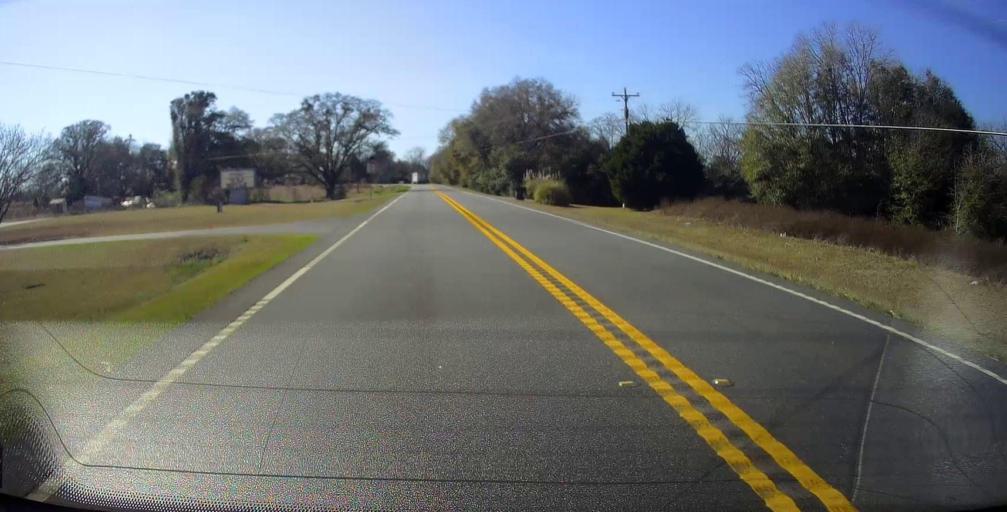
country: US
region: Georgia
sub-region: Houston County
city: Perry
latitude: 32.4468
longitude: -83.7647
